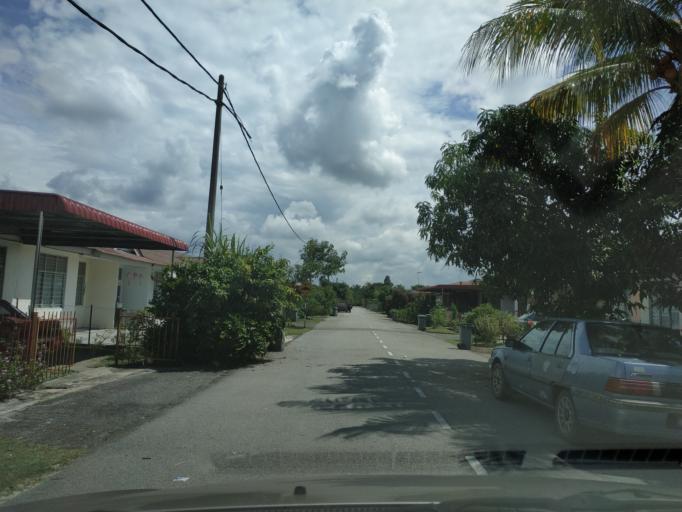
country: MY
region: Perak
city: Parit Buntar
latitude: 5.1398
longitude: 100.5955
